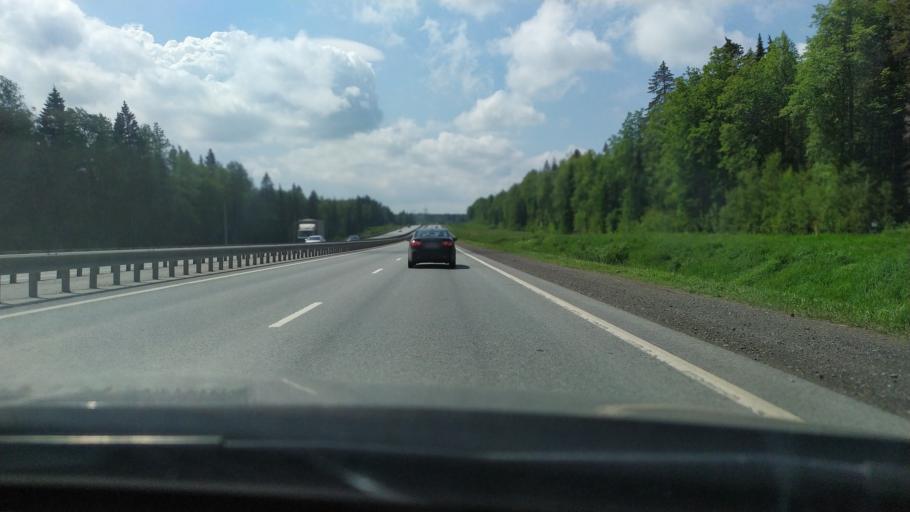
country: RU
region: Perm
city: Ferma
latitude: 58.0228
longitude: 56.4214
